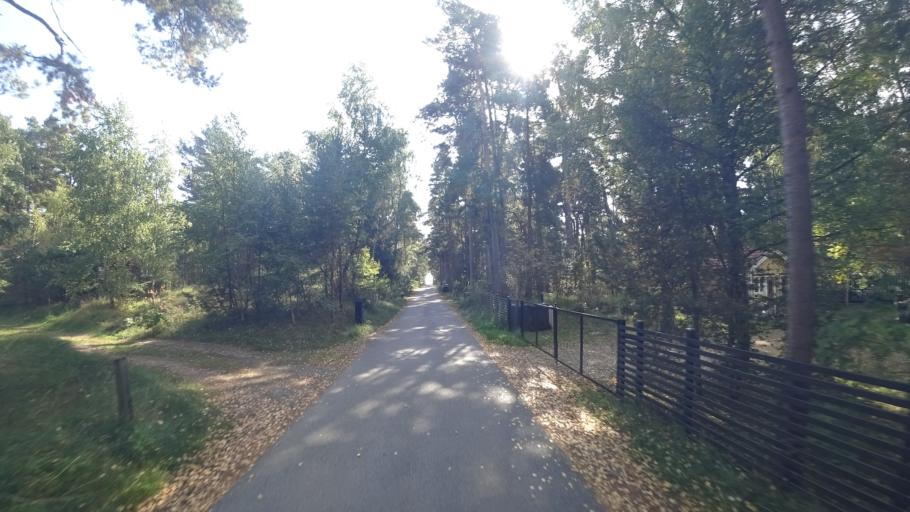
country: SE
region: Skane
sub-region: Kristianstads Kommun
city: Ahus
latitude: 55.9130
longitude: 14.3024
